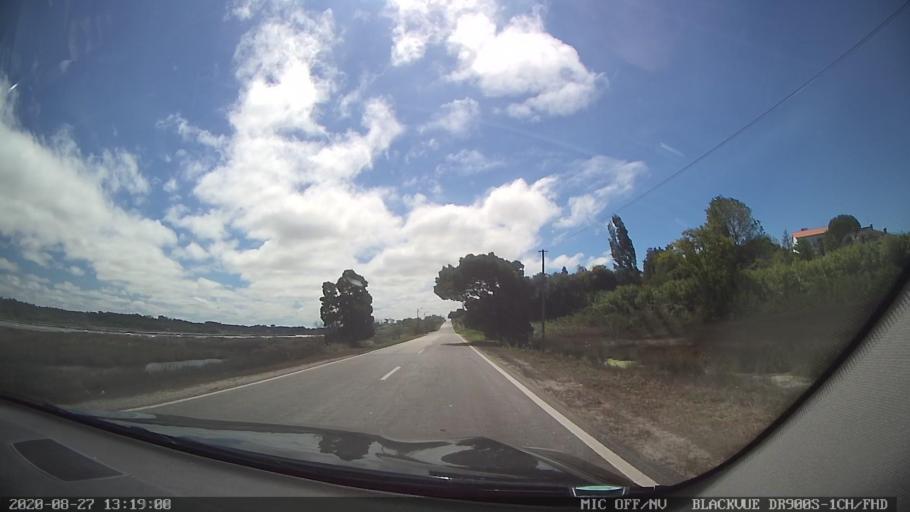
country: PT
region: Aveiro
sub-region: Vagos
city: Vagos
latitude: 40.5690
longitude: -8.6825
